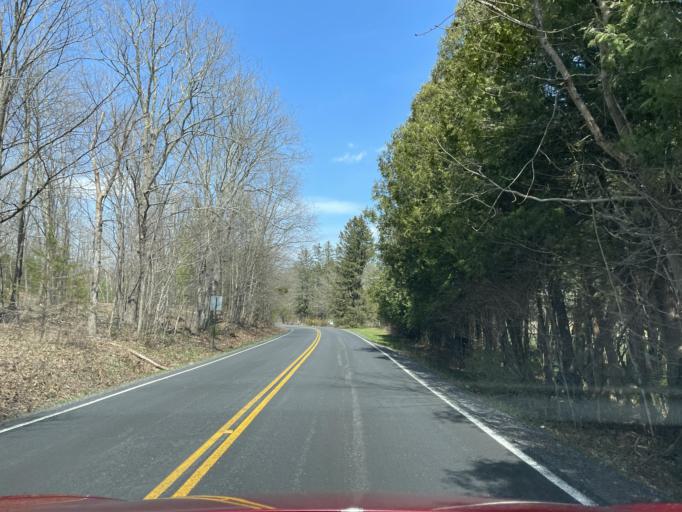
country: US
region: New York
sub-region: Ulster County
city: Manorville
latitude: 42.1108
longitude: -74.0190
